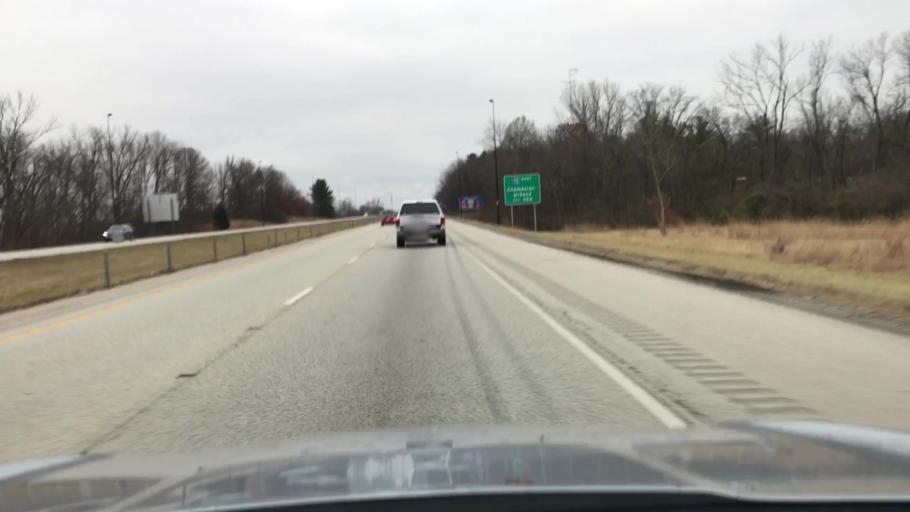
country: US
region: Illinois
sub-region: Sangamon County
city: Grandview
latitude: 39.8205
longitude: -89.5929
